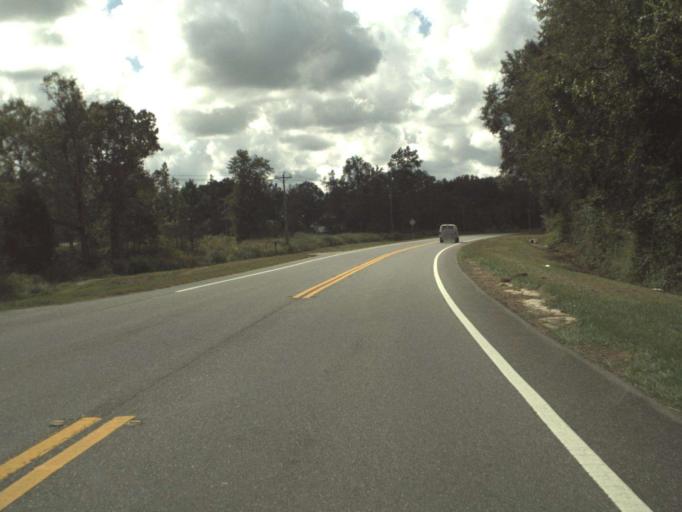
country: US
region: Florida
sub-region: Washington County
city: Chipley
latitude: 30.8185
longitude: -85.5050
